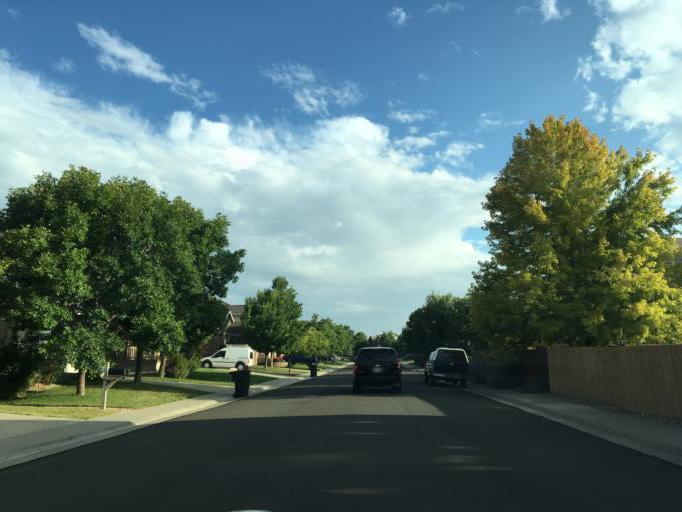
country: US
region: Colorado
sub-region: Adams County
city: Northglenn
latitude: 39.9483
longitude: -104.9530
